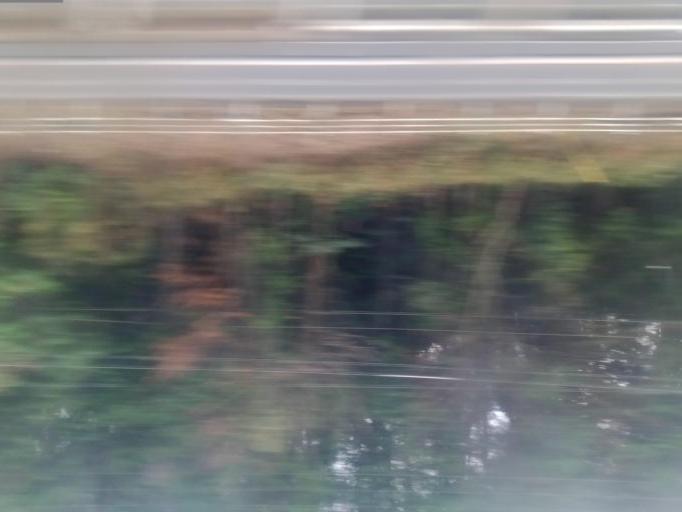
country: JP
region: Gifu
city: Nakatsugawa
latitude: 35.4474
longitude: 137.3881
